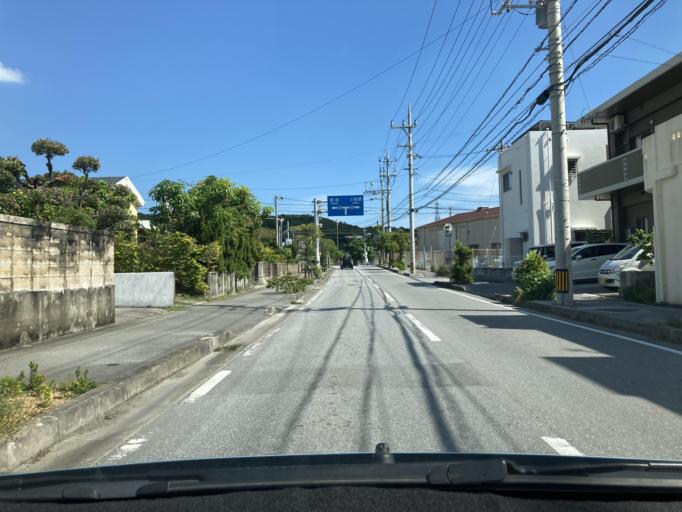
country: JP
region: Okinawa
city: Ginowan
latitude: 26.2293
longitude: 127.7528
